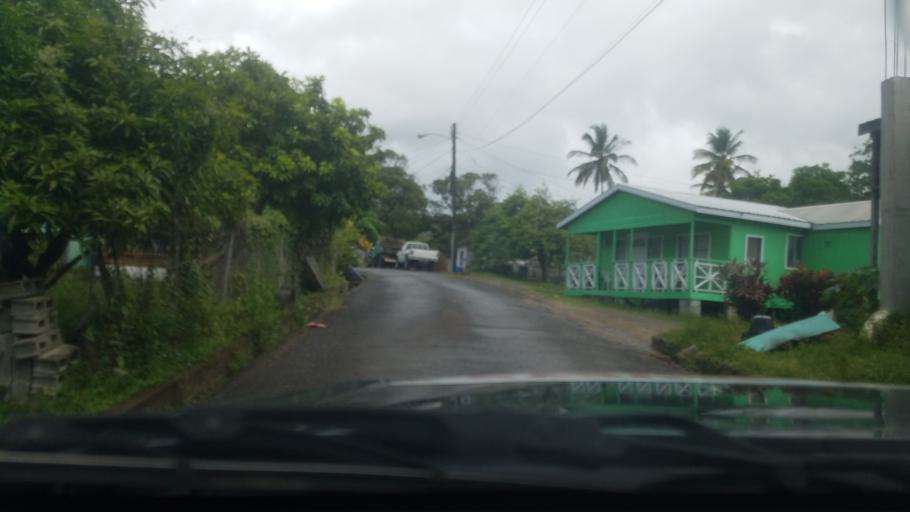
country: LC
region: Praslin
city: Praslin
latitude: 13.8749
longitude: -60.8996
